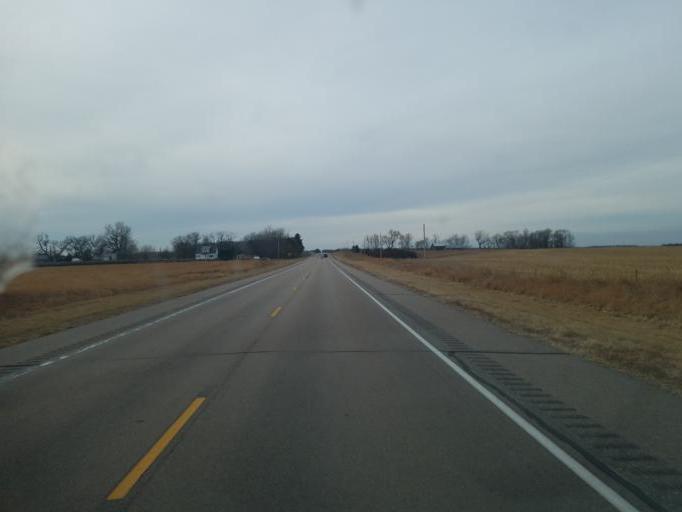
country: US
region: Nebraska
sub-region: Antelope County
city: Neligh
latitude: 42.3352
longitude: -98.1986
